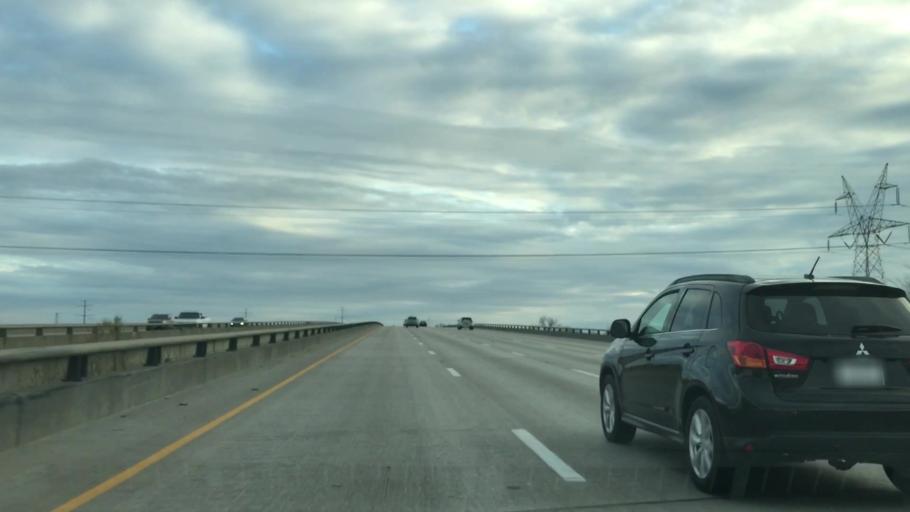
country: US
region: Texas
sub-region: Dallas County
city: Irving
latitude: 32.7888
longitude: -96.9195
